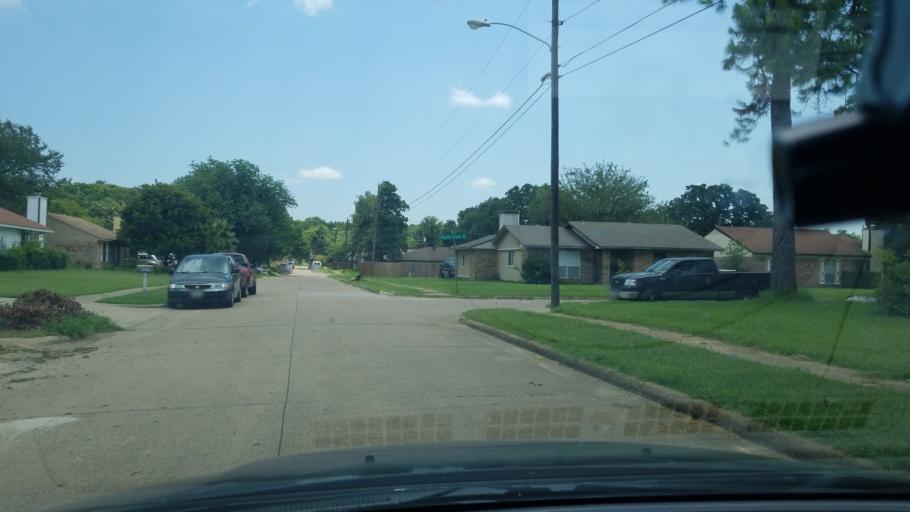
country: US
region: Texas
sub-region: Dallas County
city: Balch Springs
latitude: 32.7155
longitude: -96.6621
